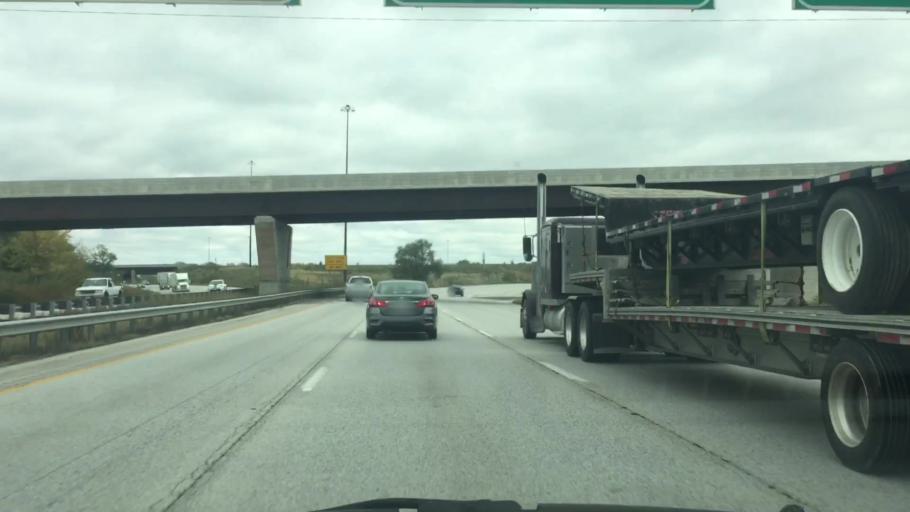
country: US
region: Iowa
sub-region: Polk County
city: Saylorville
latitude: 41.6510
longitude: -93.5827
